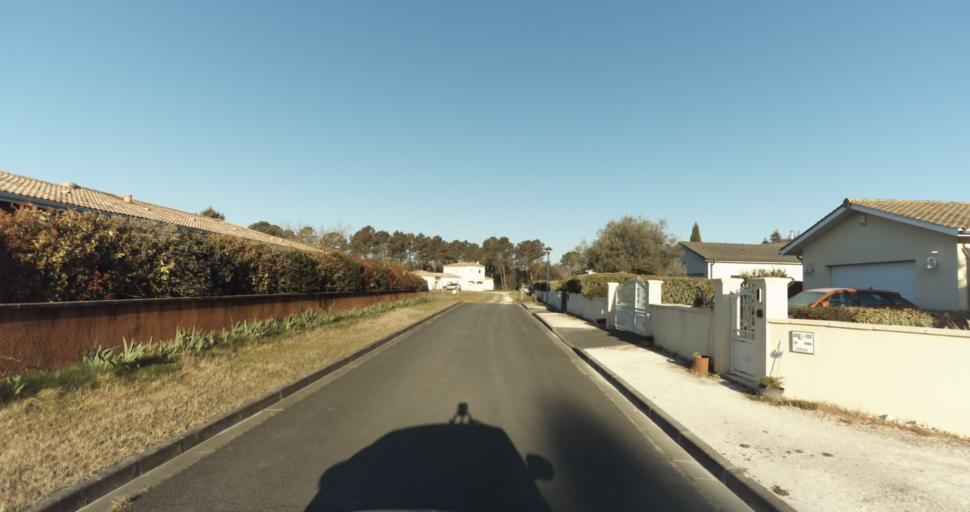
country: FR
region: Aquitaine
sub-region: Departement de la Gironde
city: Martignas-sur-Jalle
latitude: 44.8139
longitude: -0.7961
